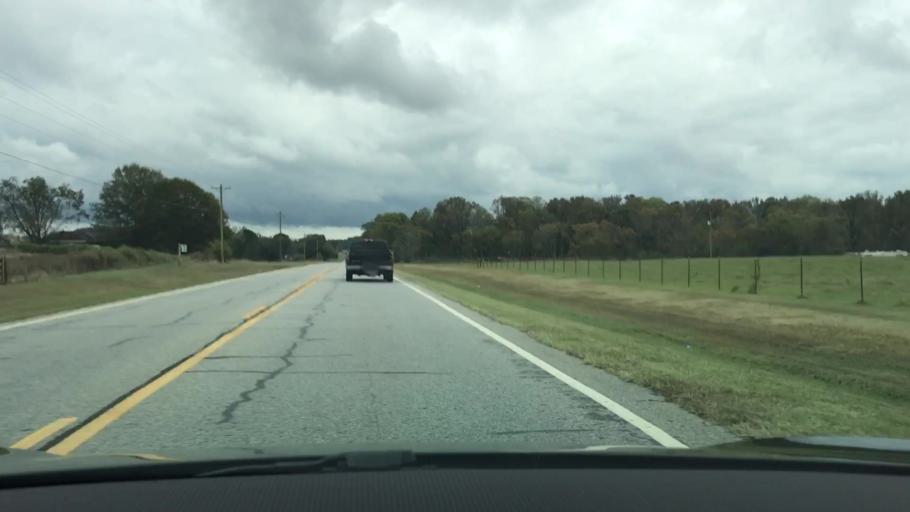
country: US
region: Georgia
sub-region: Oconee County
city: Watkinsville
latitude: 33.8253
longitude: -83.3716
